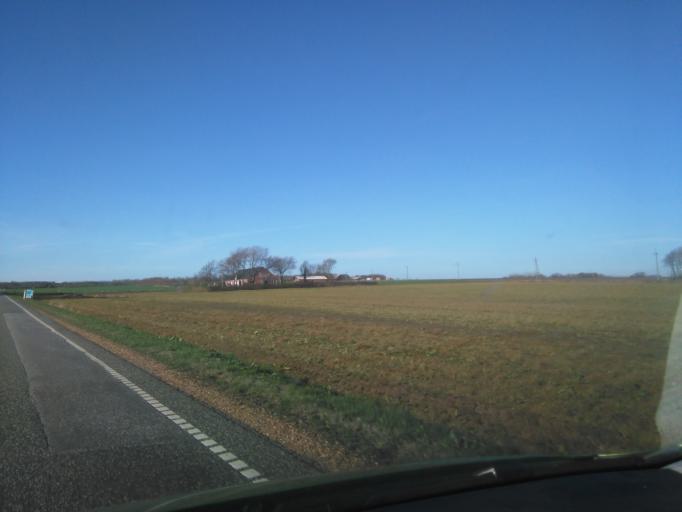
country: DK
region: Central Jutland
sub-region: Ringkobing-Skjern Kommune
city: Skjern
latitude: 56.0691
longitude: 8.5060
